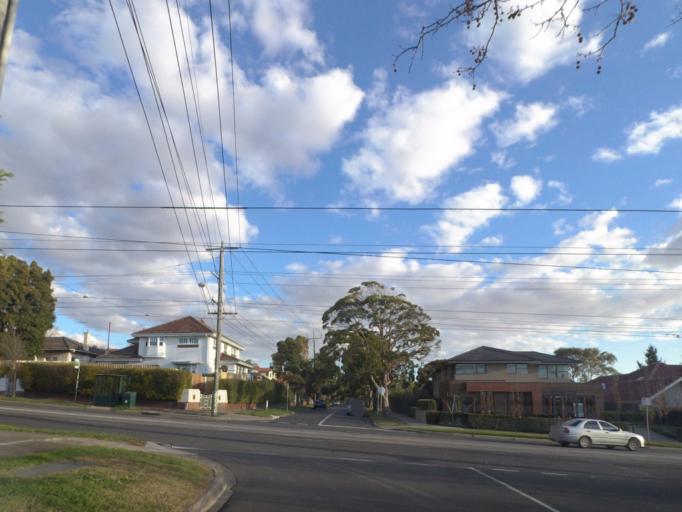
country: AU
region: Victoria
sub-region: Boroondara
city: Ashburton
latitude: -37.8492
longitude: 145.0871
